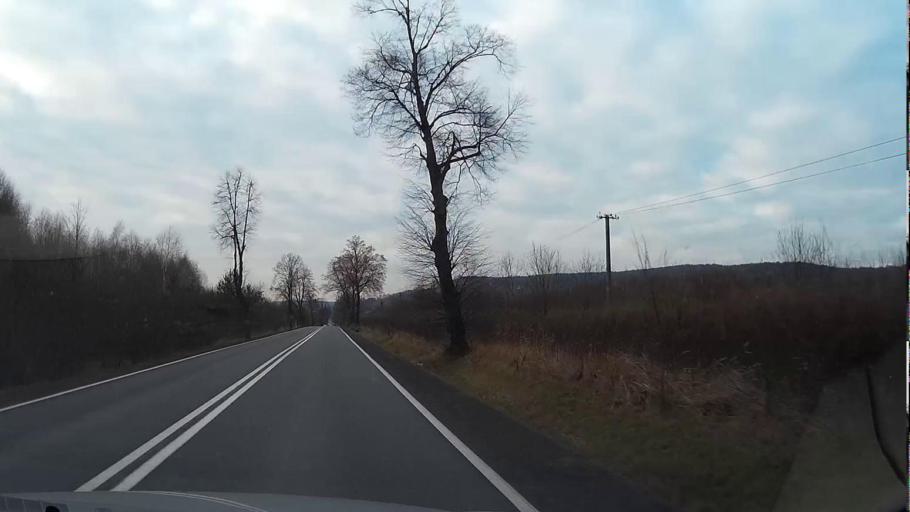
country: PL
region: Lesser Poland Voivodeship
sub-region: Powiat chrzanowski
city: Kwaczala
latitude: 50.0670
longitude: 19.4750
